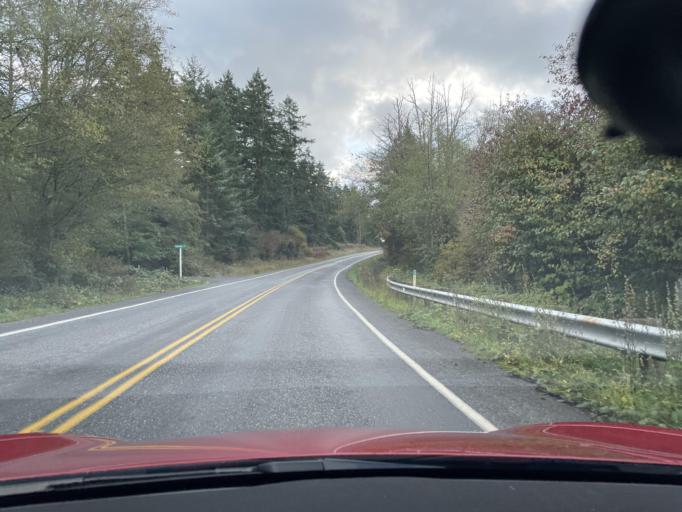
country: US
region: Washington
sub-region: San Juan County
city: Friday Harbor
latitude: 48.4973
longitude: -123.0327
